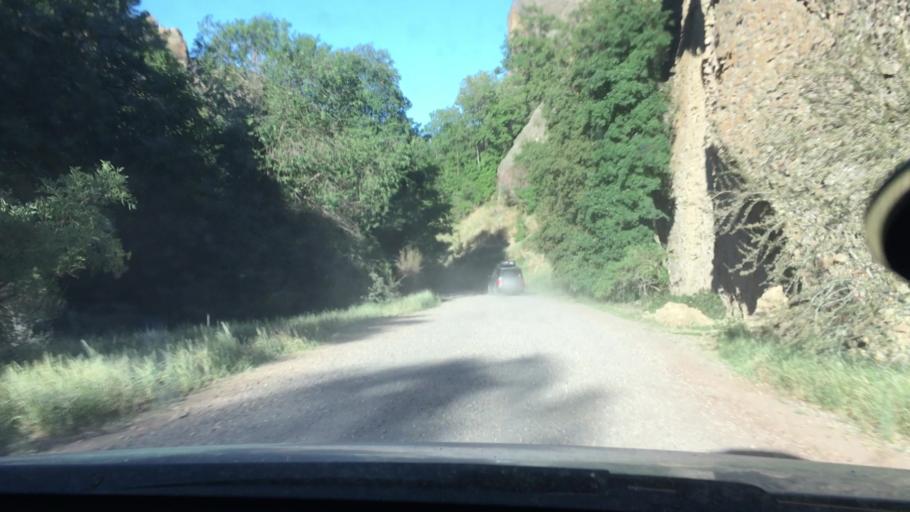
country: US
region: Utah
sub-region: Sanpete County
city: Fountain Green
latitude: 39.5549
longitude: -111.6715
